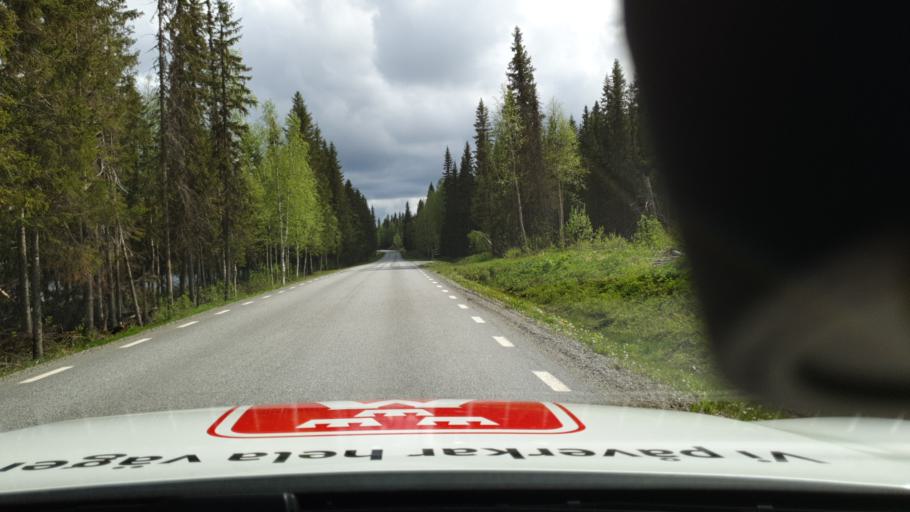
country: SE
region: Vaesterbotten
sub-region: Vilhelmina Kommun
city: Sjoberg
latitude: 64.6618
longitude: 16.3106
